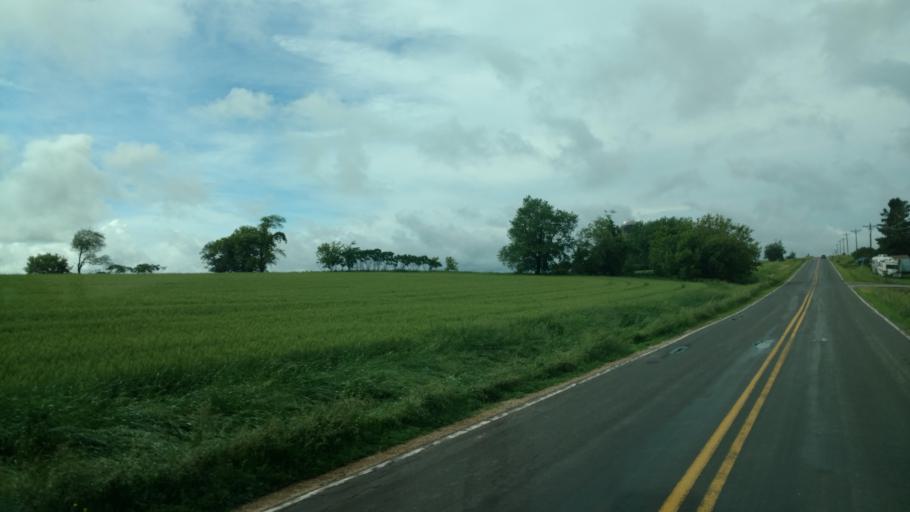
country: US
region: Wisconsin
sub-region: Vernon County
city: Hillsboro
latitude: 43.7215
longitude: -90.4478
